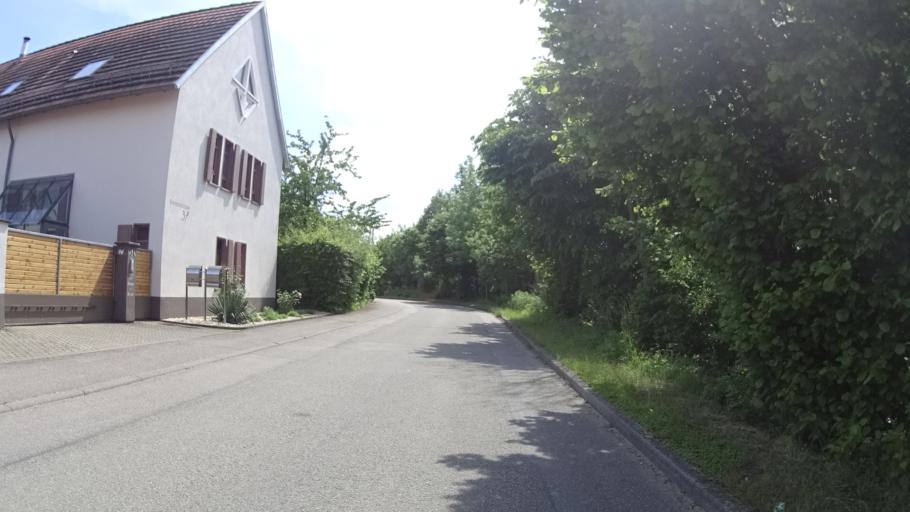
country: DE
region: Baden-Wuerttemberg
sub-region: Freiburg Region
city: Weisweil
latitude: 48.1950
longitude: 7.6728
